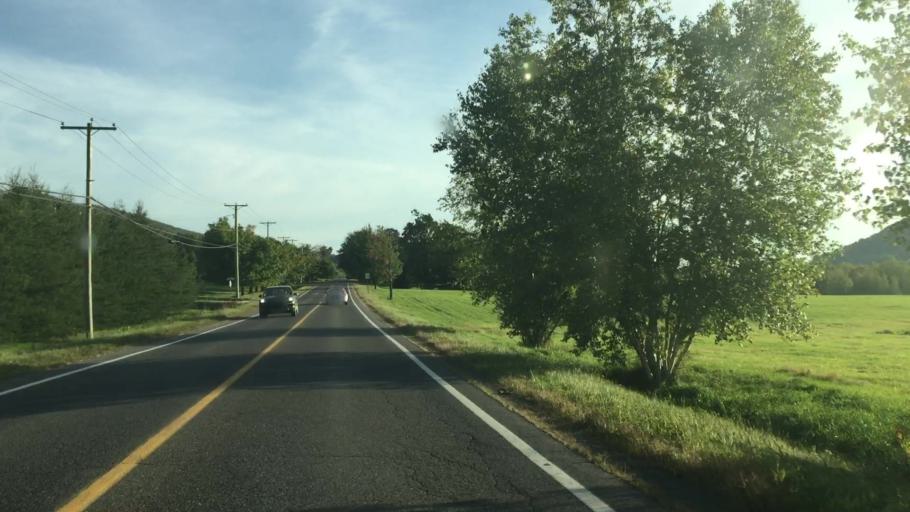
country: CA
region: Quebec
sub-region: Monteregie
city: Bromont
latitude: 45.3045
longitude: -72.6592
